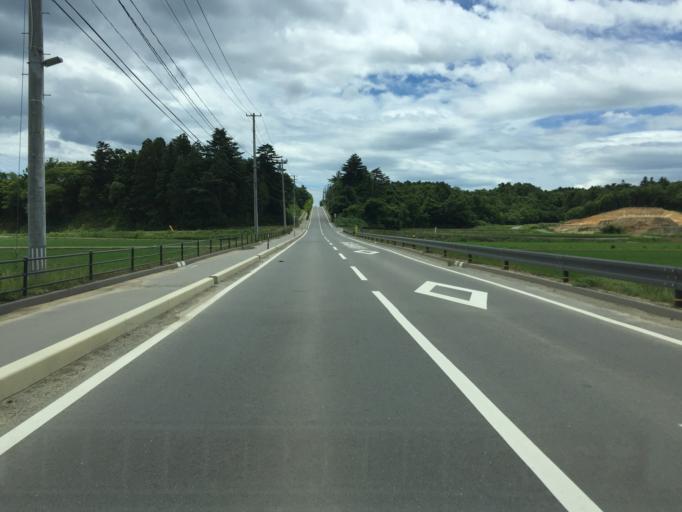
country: JP
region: Fukushima
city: Namie
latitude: 37.6608
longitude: 141.0074
